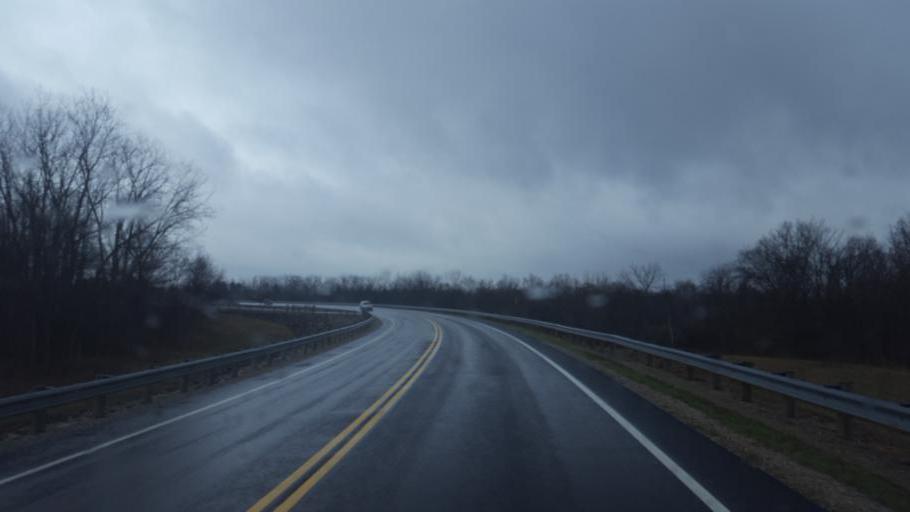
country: US
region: Ohio
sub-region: Delaware County
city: Lewis Center
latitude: 40.1848
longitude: -82.9758
